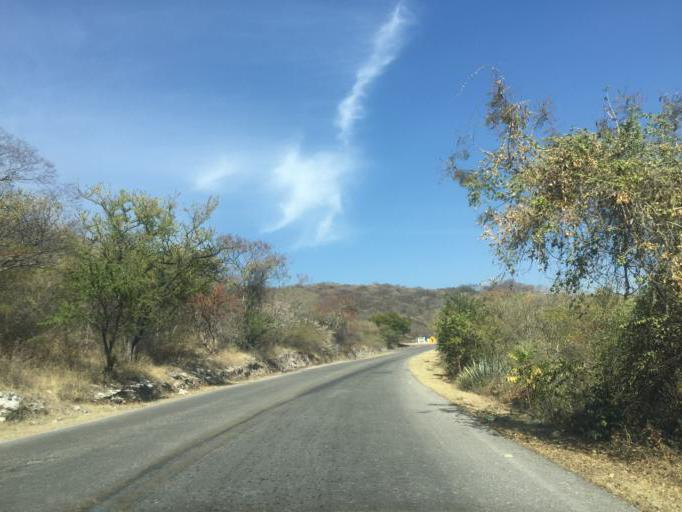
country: MX
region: Morelos
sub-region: Miacatlan
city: Xochicalco (Cirenio Longares)
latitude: 18.8027
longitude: -99.2948
